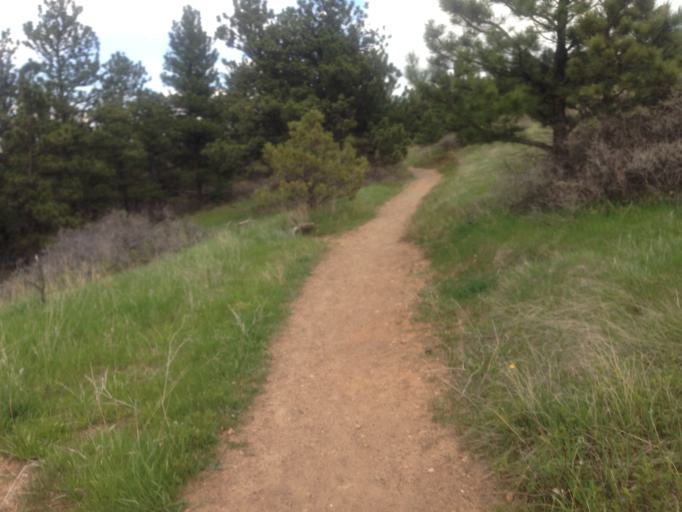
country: US
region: Colorado
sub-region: Boulder County
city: Superior
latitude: 39.9510
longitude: -105.2225
